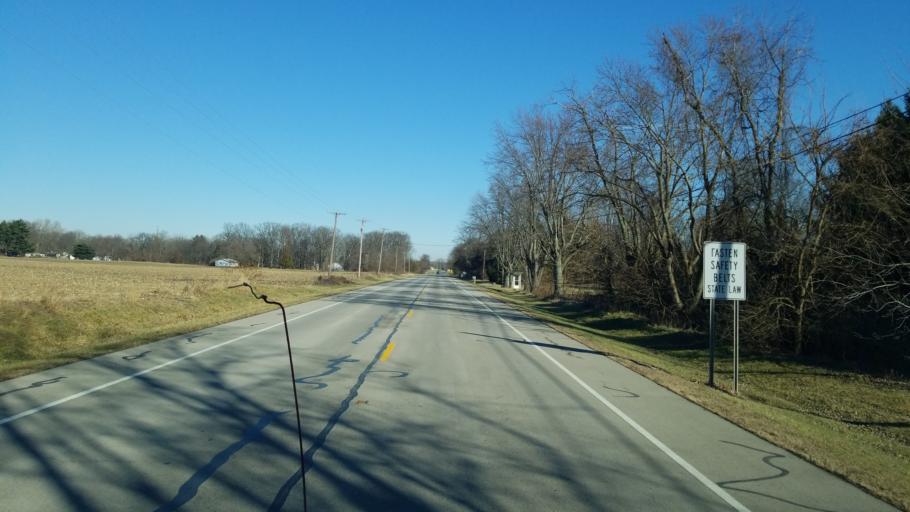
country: US
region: Ohio
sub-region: Lucas County
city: Whitehouse
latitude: 41.4476
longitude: -83.7980
